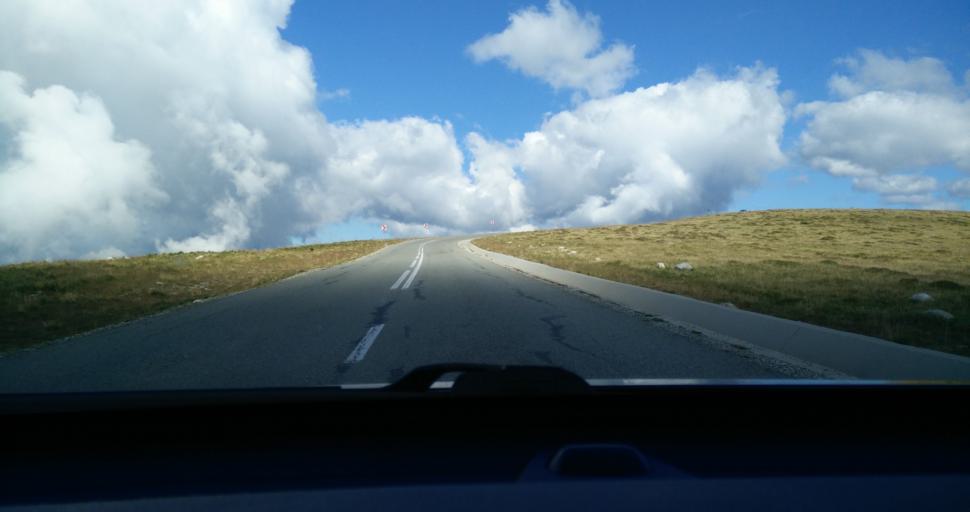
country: RO
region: Gorj
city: Novaci-Straini
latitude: 45.2627
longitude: 23.6866
